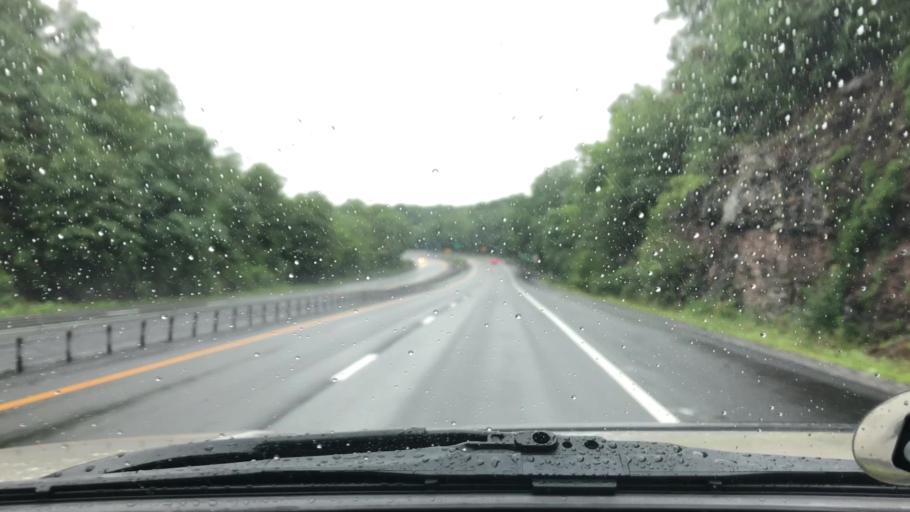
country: US
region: New York
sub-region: Greene County
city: Cairo
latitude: 42.3055
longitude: -73.9998
